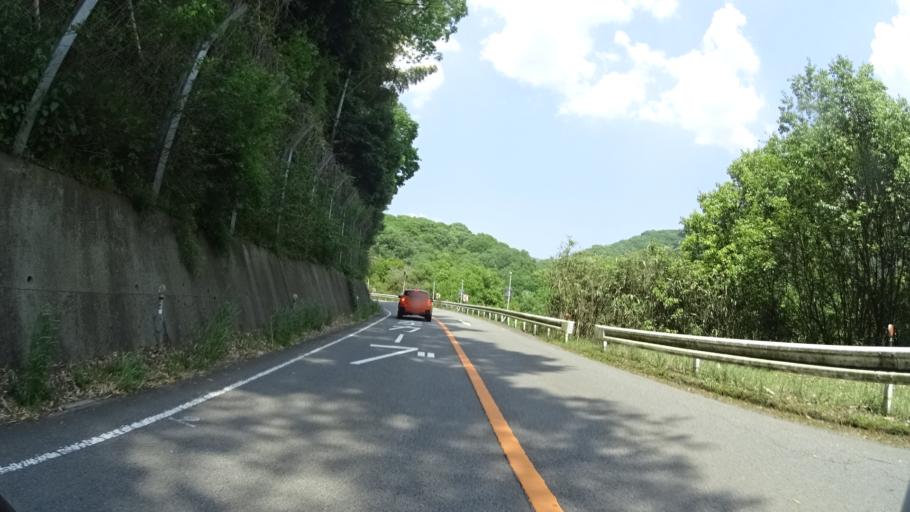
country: JP
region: Ehime
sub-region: Shikoku-chuo Shi
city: Matsuyama
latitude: 33.8841
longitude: 132.8365
